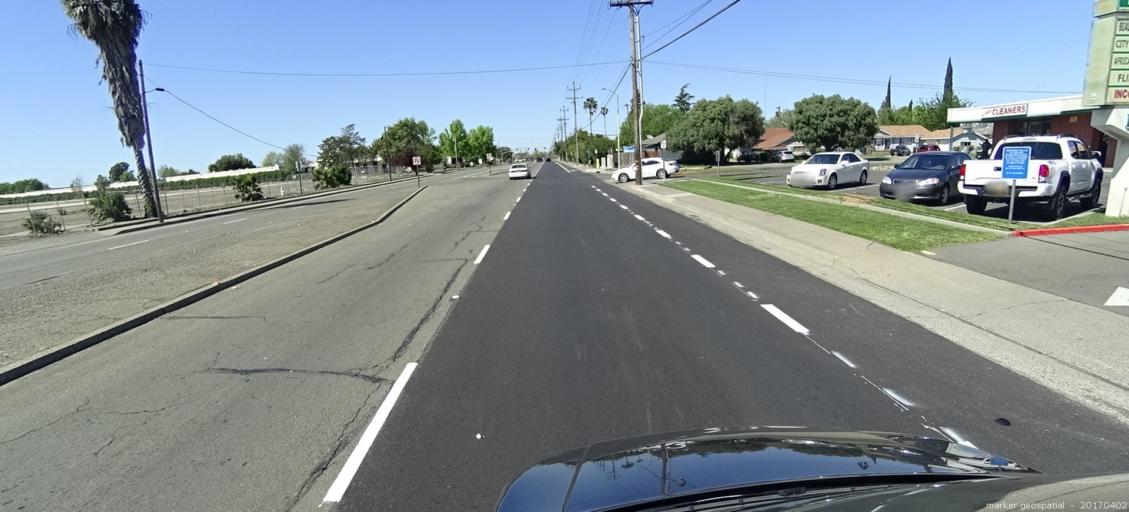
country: US
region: California
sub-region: Sacramento County
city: Parkway
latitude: 38.4975
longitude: -121.4600
